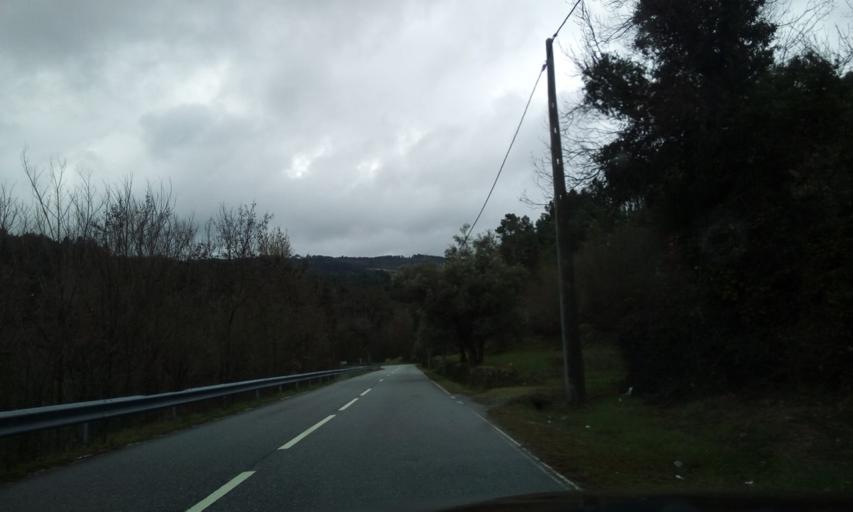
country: PT
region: Guarda
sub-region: Fornos de Algodres
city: Fornos de Algodres
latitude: 40.6100
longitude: -7.5760
